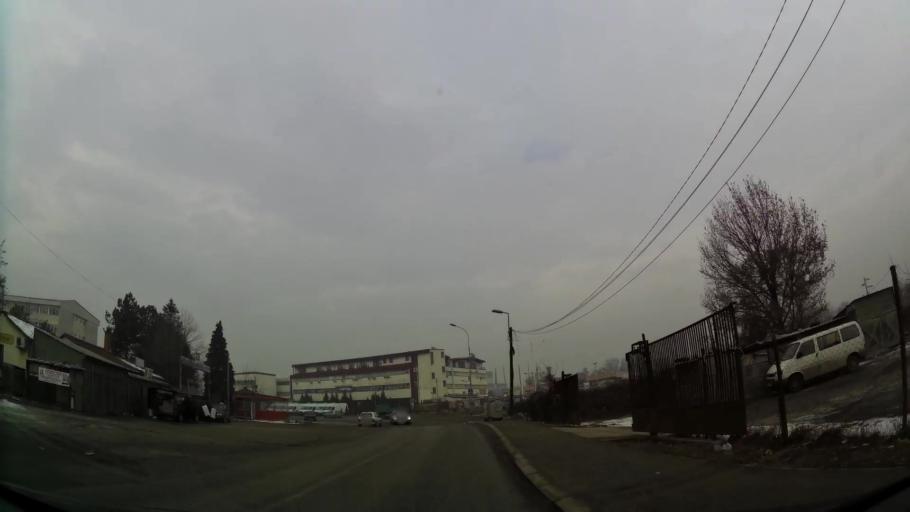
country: MK
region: Kisela Voda
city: Usje
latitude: 41.9968
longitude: 21.4884
